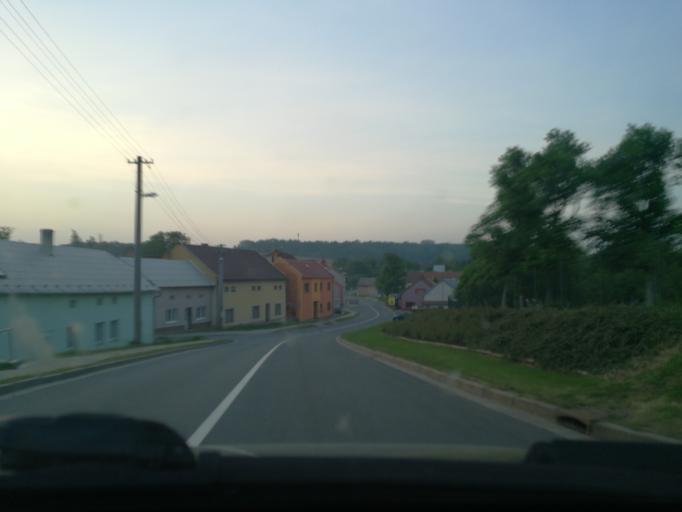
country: CZ
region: Zlin
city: Tlumacov
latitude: 49.2752
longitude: 17.5490
